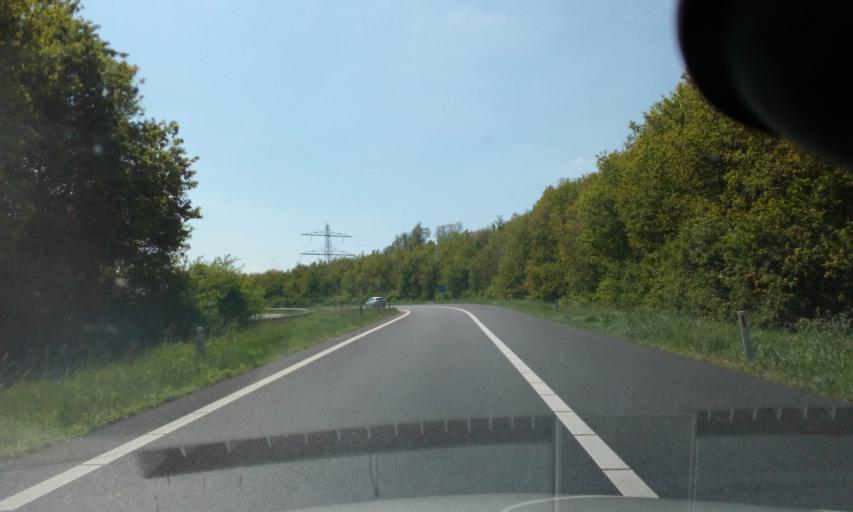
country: NL
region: North Brabant
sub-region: Gemeente Cuijk
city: Cuijk
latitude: 51.7723
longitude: 5.8358
